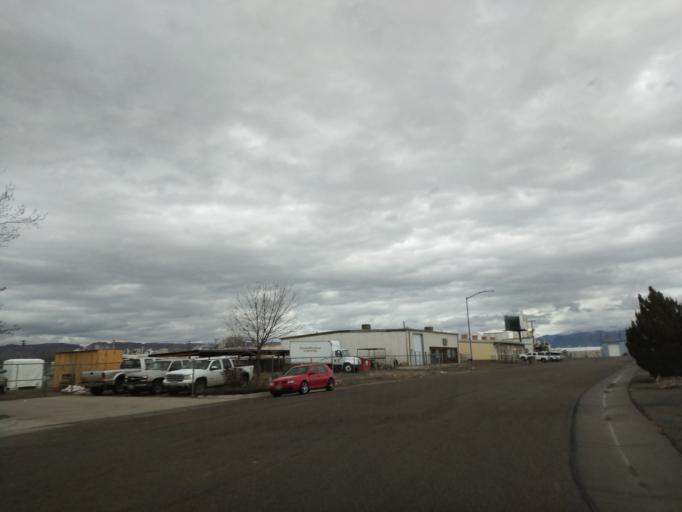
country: US
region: Colorado
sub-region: Mesa County
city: Grand Junction
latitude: 39.0722
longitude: -108.5260
